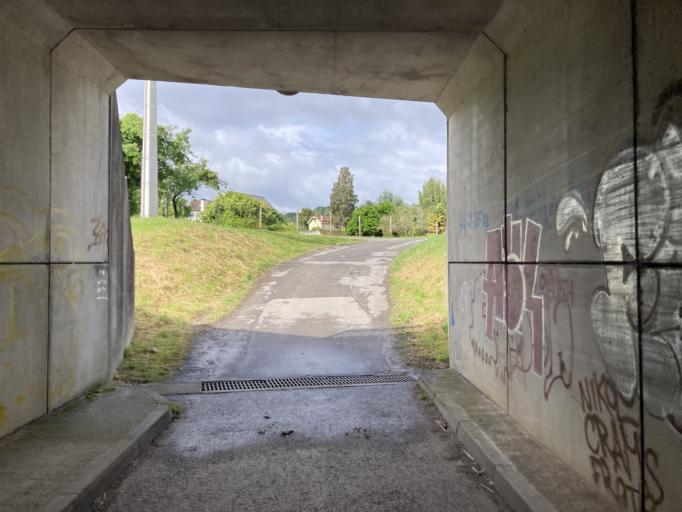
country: FR
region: Aquitaine
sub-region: Departement des Pyrenees-Atlantiques
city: Artiguelouve
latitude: 43.3054
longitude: -0.4394
